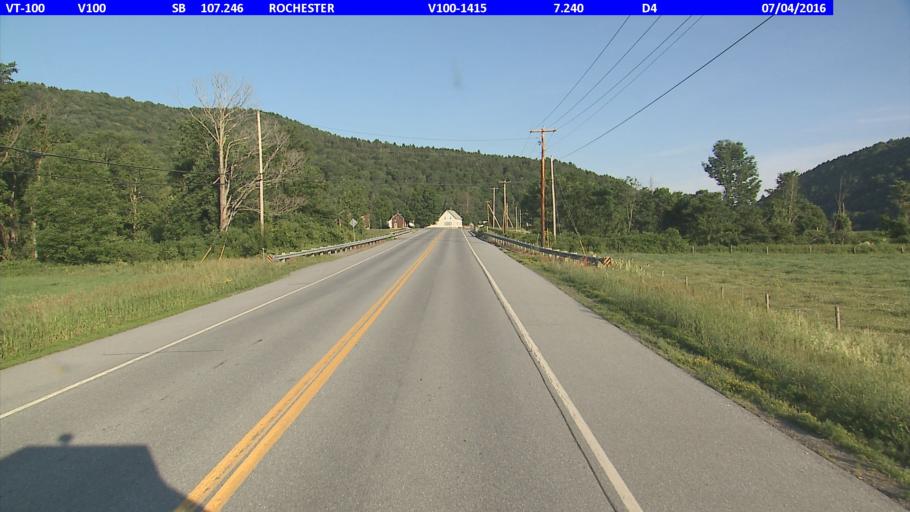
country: US
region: Vermont
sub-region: Orange County
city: Randolph
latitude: 43.8984
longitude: -72.8223
